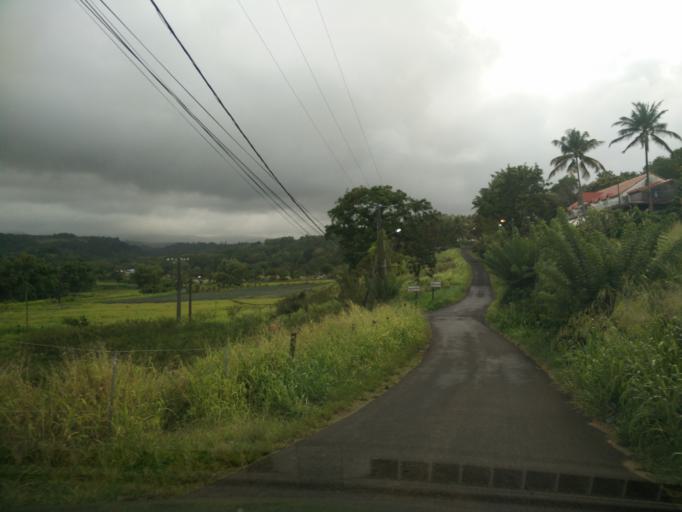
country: GP
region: Guadeloupe
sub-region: Guadeloupe
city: Petit-Bourg
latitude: 16.1787
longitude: -61.6176
